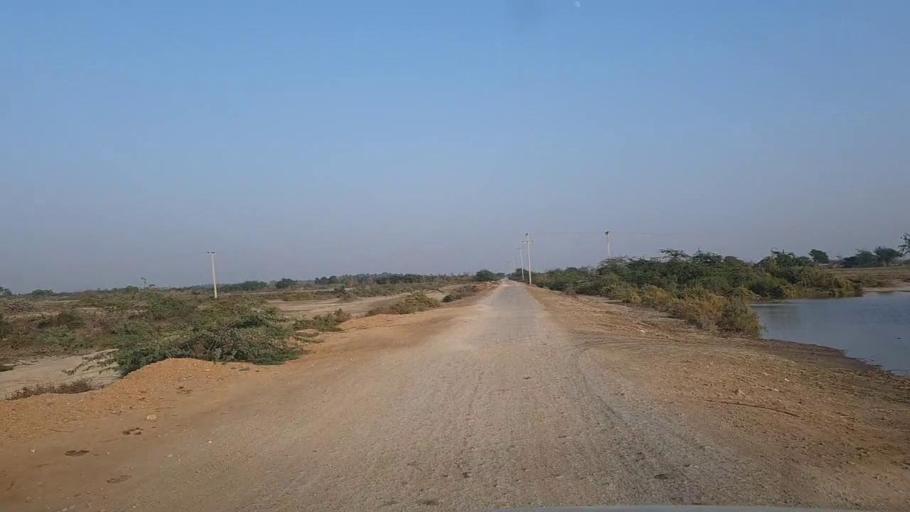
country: PK
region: Sindh
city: Keti Bandar
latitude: 24.2805
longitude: 67.6149
